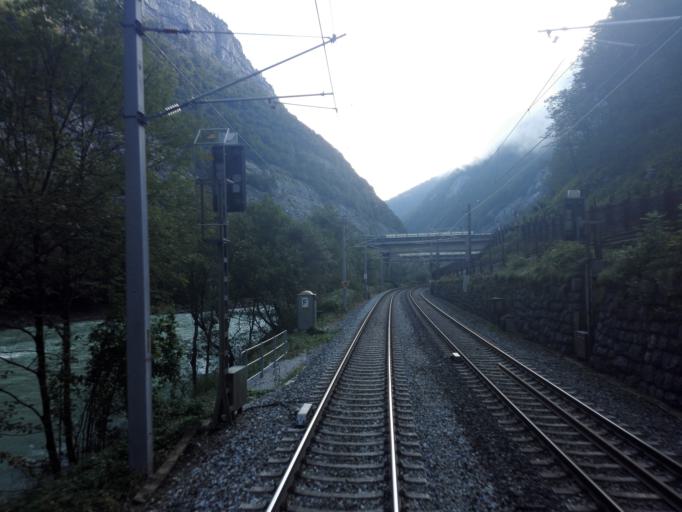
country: AT
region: Salzburg
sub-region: Politischer Bezirk Hallein
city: Golling an der Salzach
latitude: 47.5652
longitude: 13.1709
